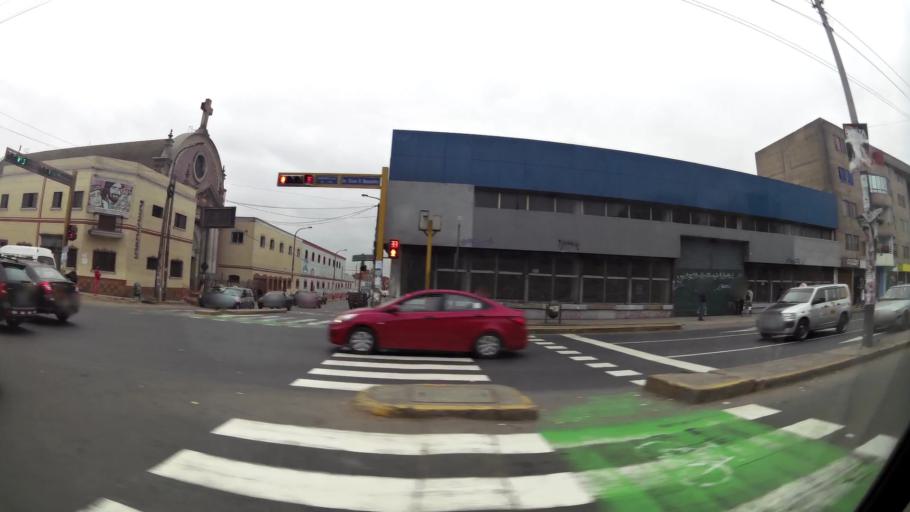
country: PE
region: Lima
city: Lima
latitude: -12.0463
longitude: -77.0466
